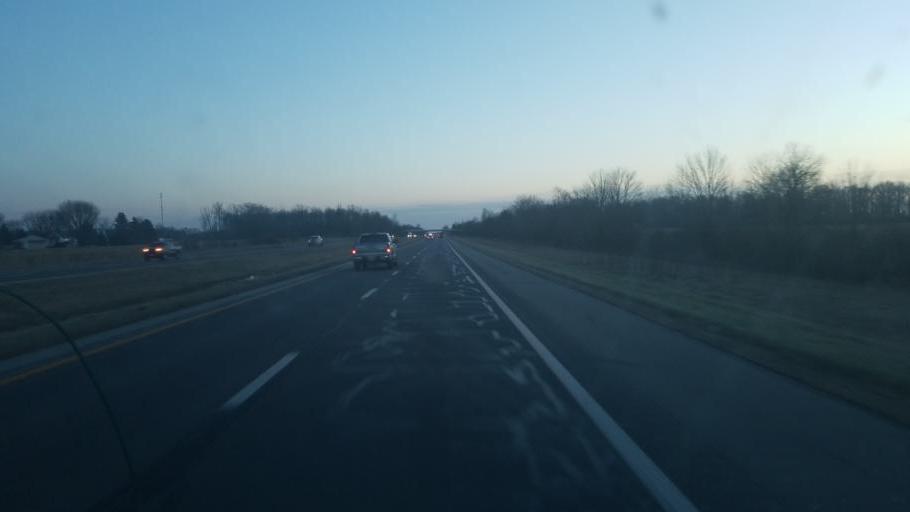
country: US
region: Ohio
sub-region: Marion County
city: Marion
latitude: 40.5419
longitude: -83.0747
